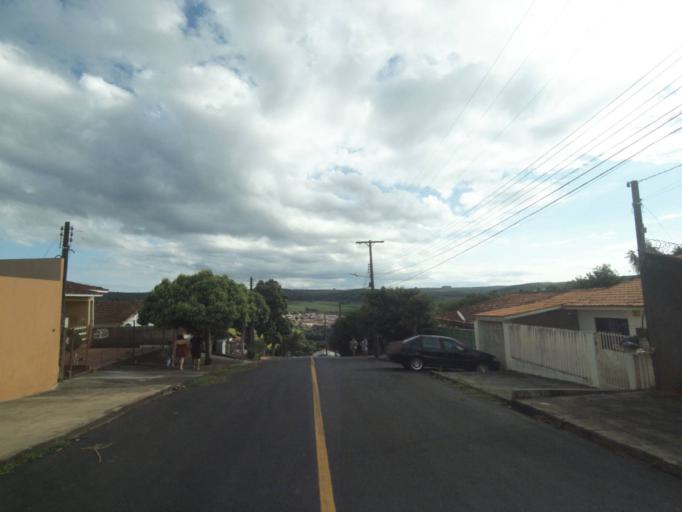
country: BR
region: Parana
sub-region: Telemaco Borba
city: Telemaco Borba
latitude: -24.3397
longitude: -50.6123
